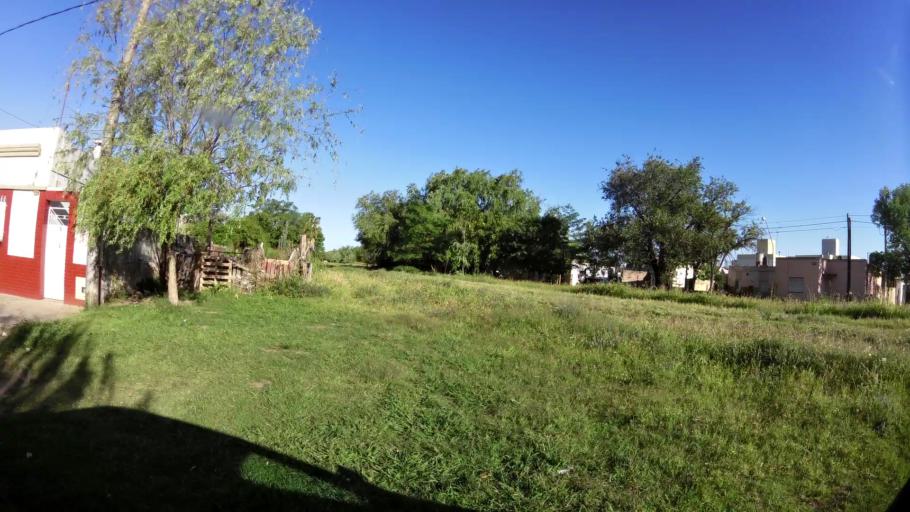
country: AR
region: Cordoba
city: San Francisco
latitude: -31.4380
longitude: -62.0913
